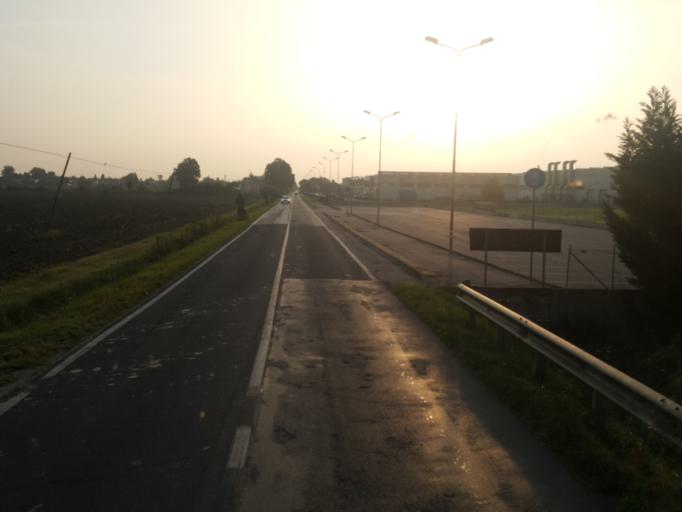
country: IT
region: Emilia-Romagna
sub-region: Provincia di Ravenna
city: Lavezzola
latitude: 44.5571
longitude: 11.8599
